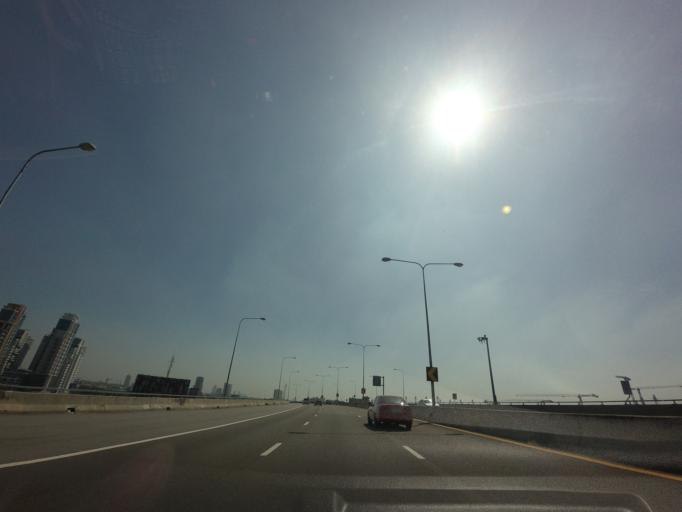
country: TH
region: Bangkok
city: Phra Khanong
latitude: 13.6736
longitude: 100.6063
